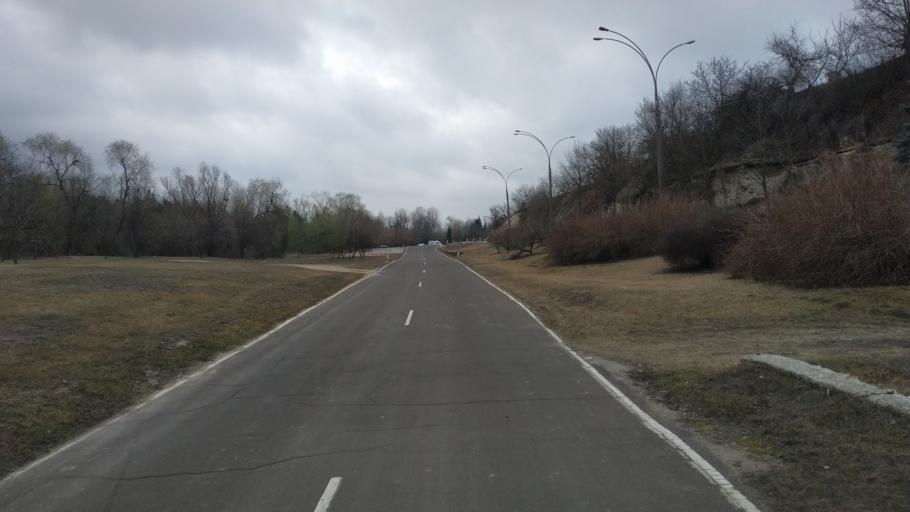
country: MD
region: Laloveni
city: Ialoveni
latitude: 46.9232
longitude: 28.8174
